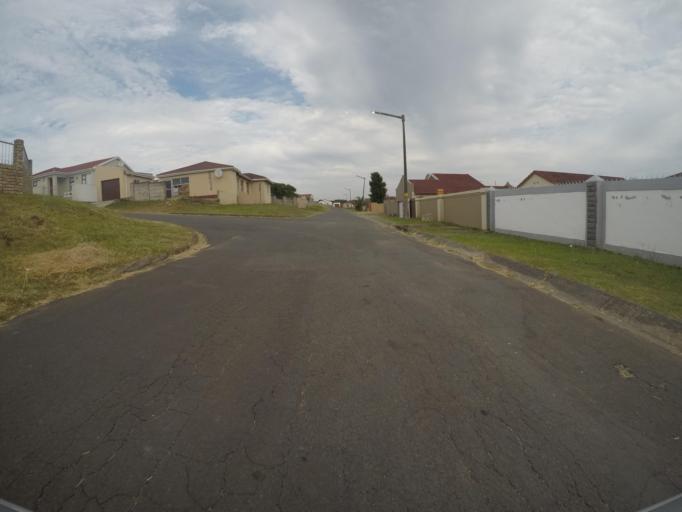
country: ZA
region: Eastern Cape
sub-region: Buffalo City Metropolitan Municipality
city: East London
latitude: -32.9759
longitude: 27.8596
